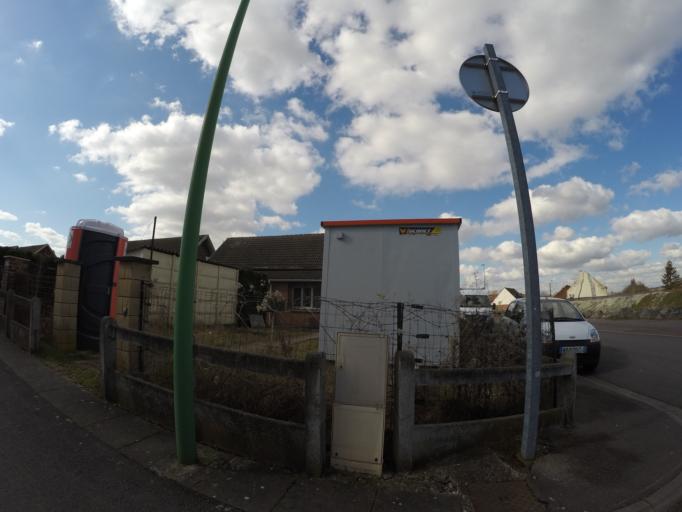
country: FR
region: Nord-Pas-de-Calais
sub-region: Departement du Pas-de-Calais
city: Mazingarbe
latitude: 50.4614
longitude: 2.7232
